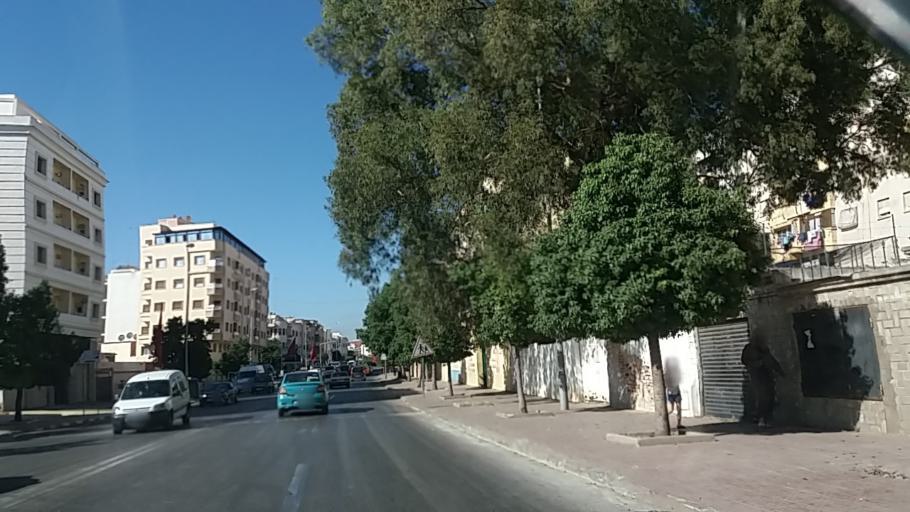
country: MA
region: Tanger-Tetouan
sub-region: Tanger-Assilah
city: Tangier
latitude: 35.7725
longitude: -5.8298
